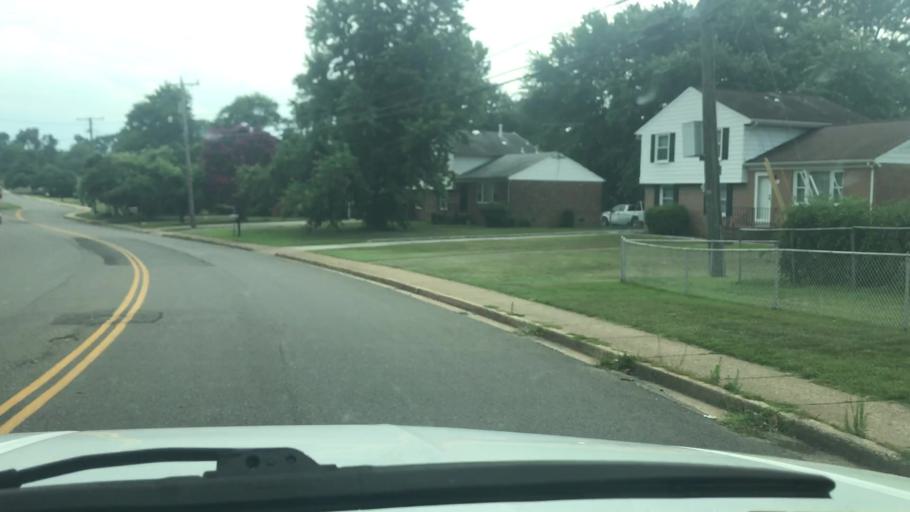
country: US
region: Virginia
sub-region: Henrico County
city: Laurel
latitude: 37.6417
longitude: -77.5440
